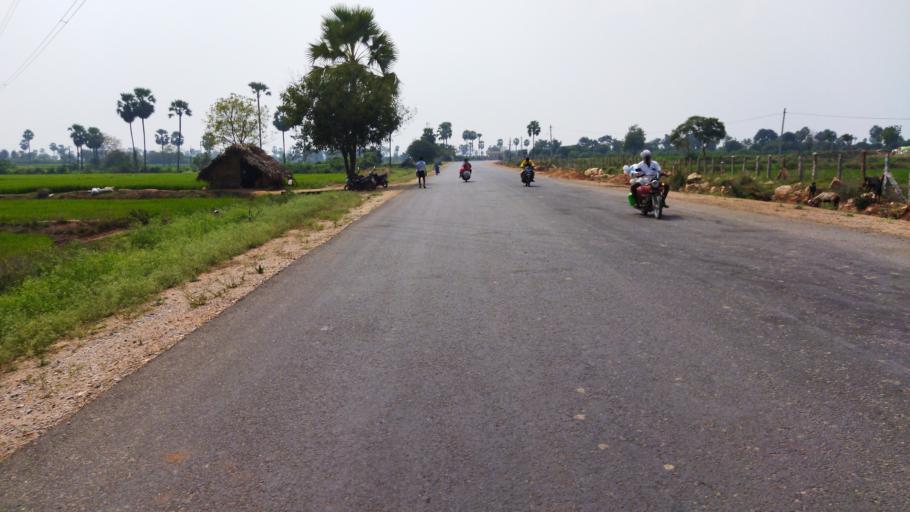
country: IN
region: Telangana
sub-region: Nalgonda
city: Nalgonda
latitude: 17.1143
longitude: 79.3609
